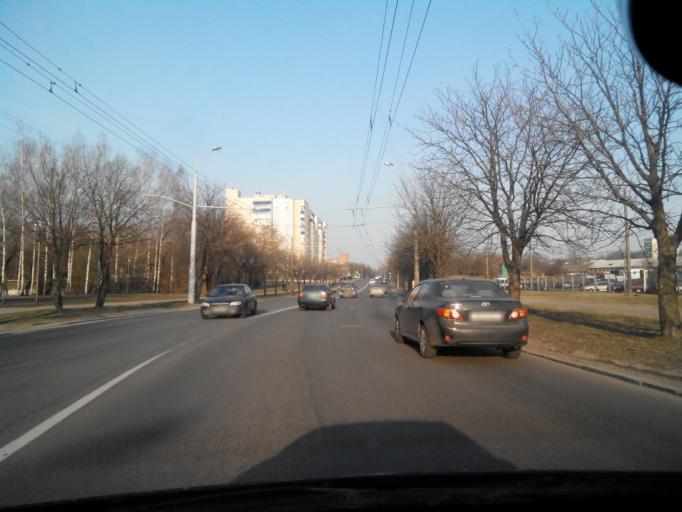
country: BY
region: Minsk
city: Minsk
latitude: 53.8992
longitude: 27.5097
